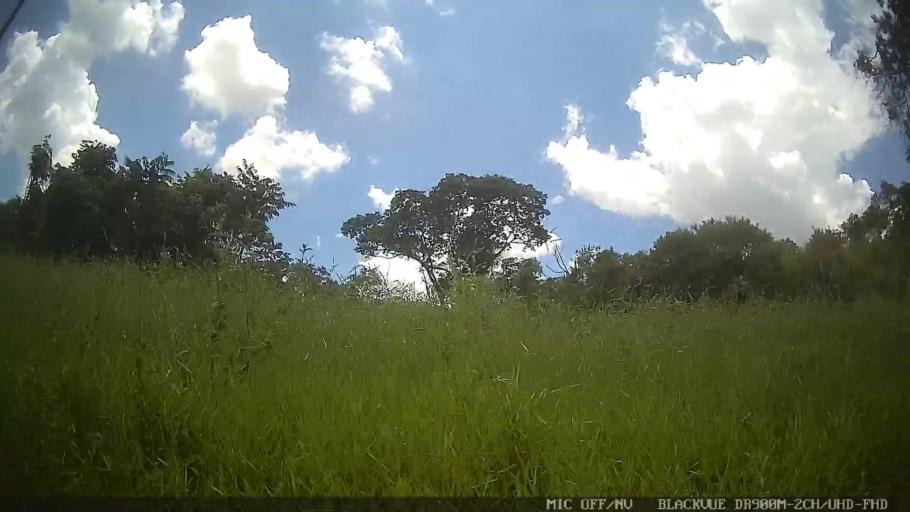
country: BR
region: Sao Paulo
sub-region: Atibaia
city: Atibaia
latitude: -23.1311
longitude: -46.6331
